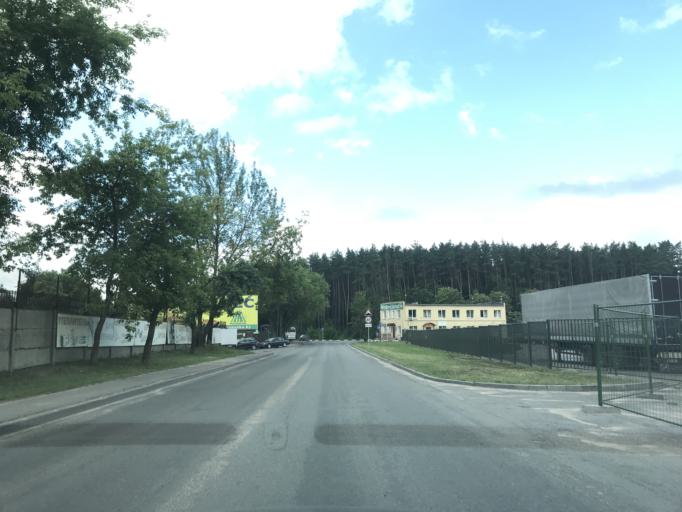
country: BY
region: Minsk
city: Borovlyany
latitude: 53.9587
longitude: 27.6905
